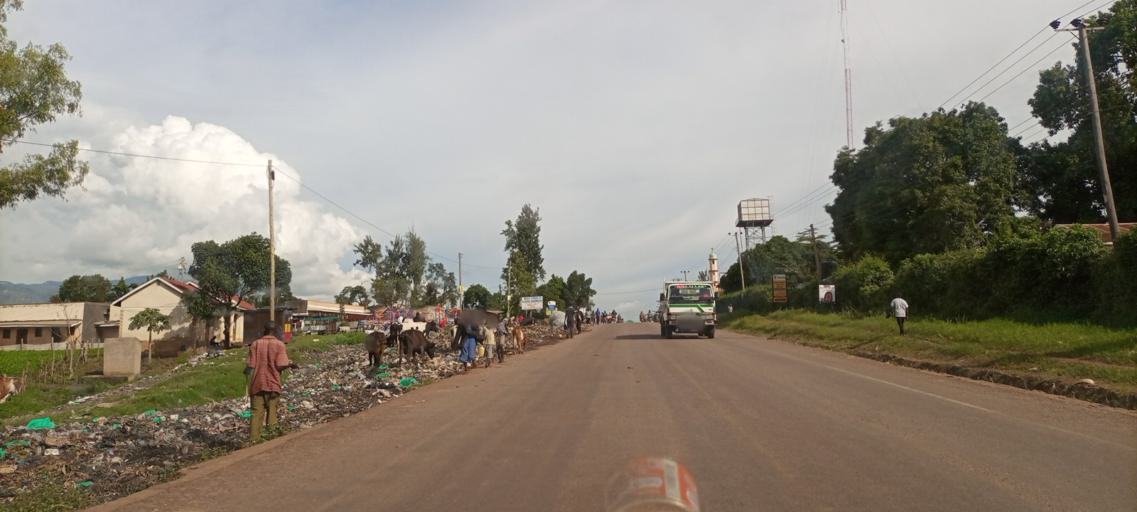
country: UG
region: Eastern Region
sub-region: Mbale District
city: Mbale
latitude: 1.1006
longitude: 34.1746
